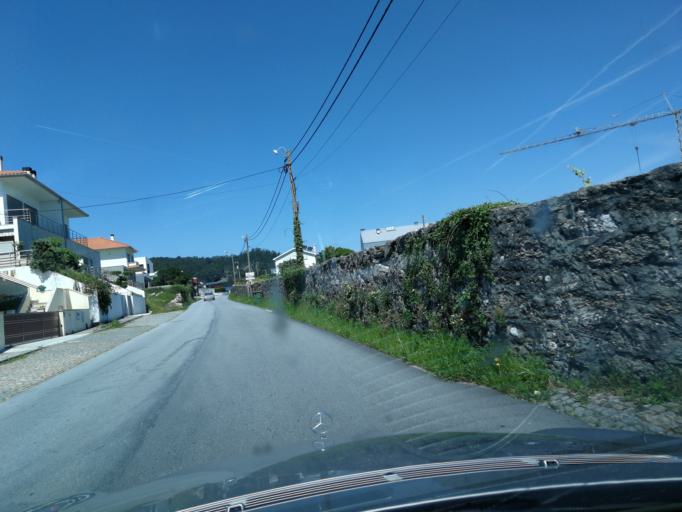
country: PT
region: Viana do Castelo
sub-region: Viana do Castelo
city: Meadela
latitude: 41.7165
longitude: -8.7987
